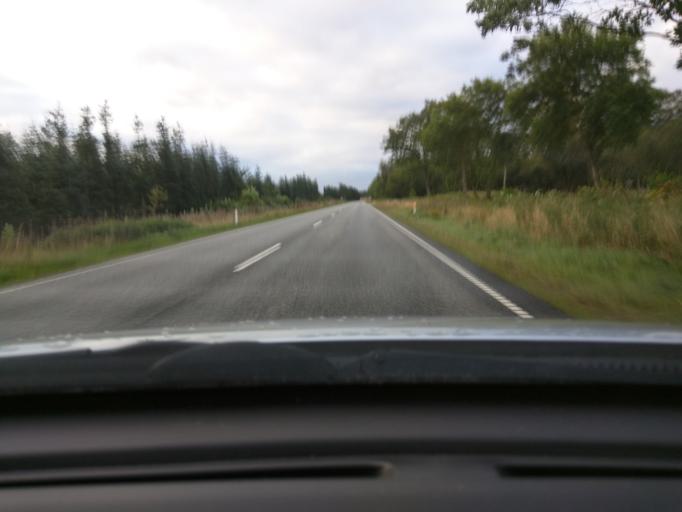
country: DK
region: Central Jutland
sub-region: Ikast-Brande Kommune
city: Bording Kirkeby
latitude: 56.2568
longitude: 9.3177
